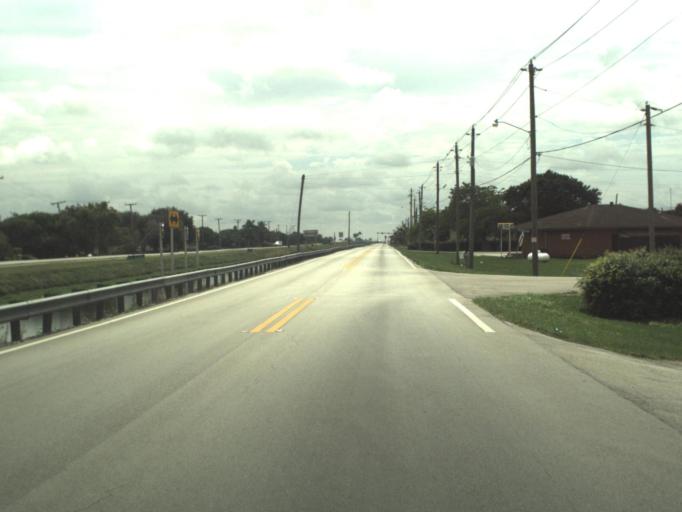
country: US
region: Florida
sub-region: Palm Beach County
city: Belle Glade
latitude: 26.6849
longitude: -80.6656
